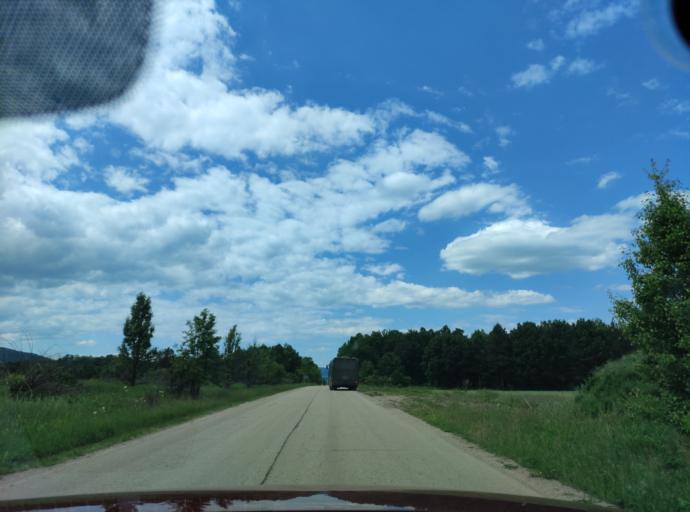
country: BG
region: Montana
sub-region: Obshtina Berkovitsa
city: Berkovitsa
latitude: 43.3662
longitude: 23.0856
